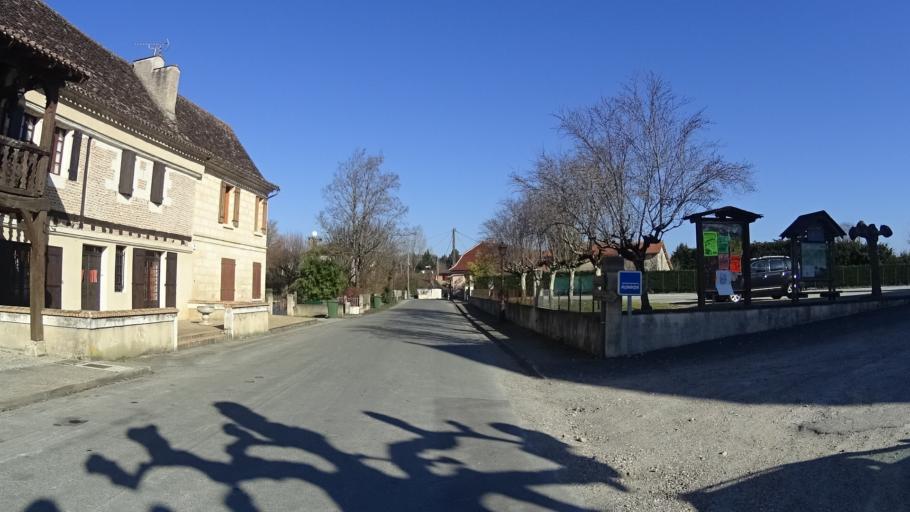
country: FR
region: Aquitaine
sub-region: Departement de la Dordogne
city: Montpon-Menesterol
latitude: 45.0371
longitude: 0.2538
